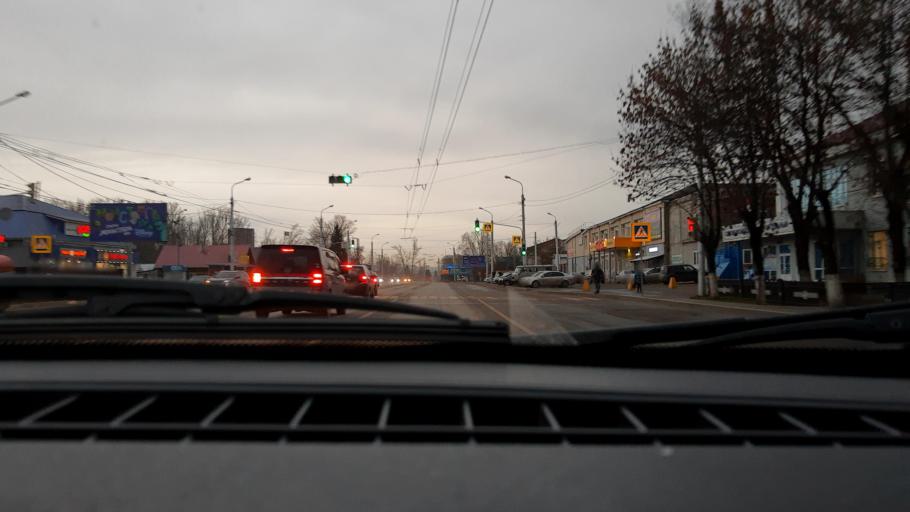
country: RU
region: Bashkortostan
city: Mikhaylovka
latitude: 54.7792
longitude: 55.8897
